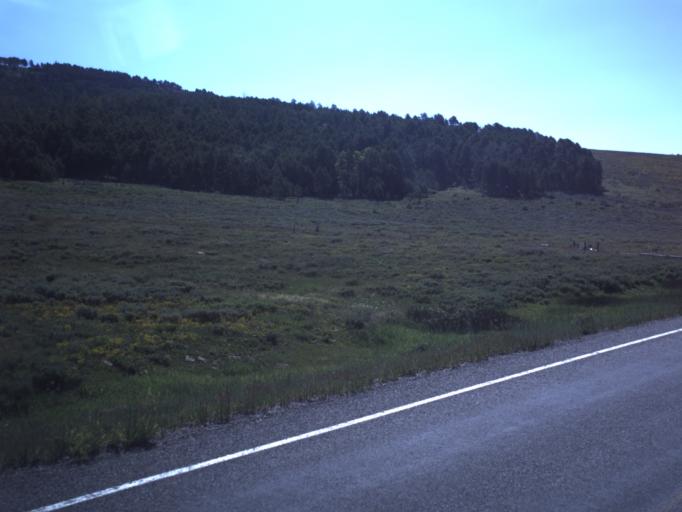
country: US
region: Utah
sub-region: Sanpete County
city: Fairview
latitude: 39.6648
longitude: -111.3020
